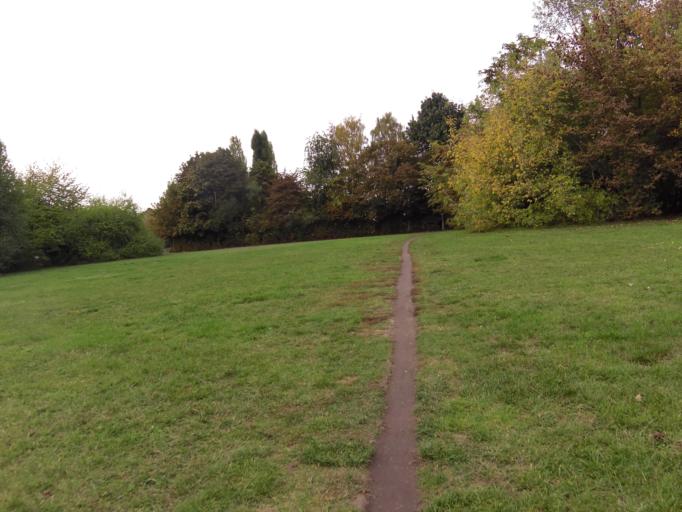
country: DE
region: Saxony
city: Leipzig
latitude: 51.3214
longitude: 12.3872
